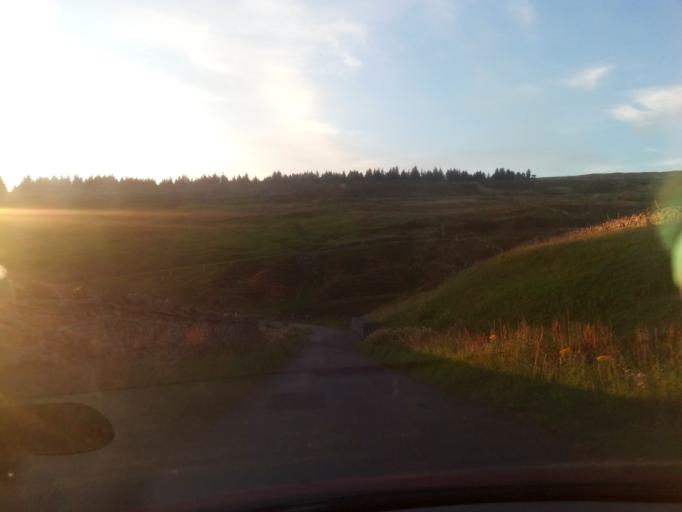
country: GB
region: England
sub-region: Northumberland
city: Bardon Mill
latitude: 54.7979
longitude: -2.3451
